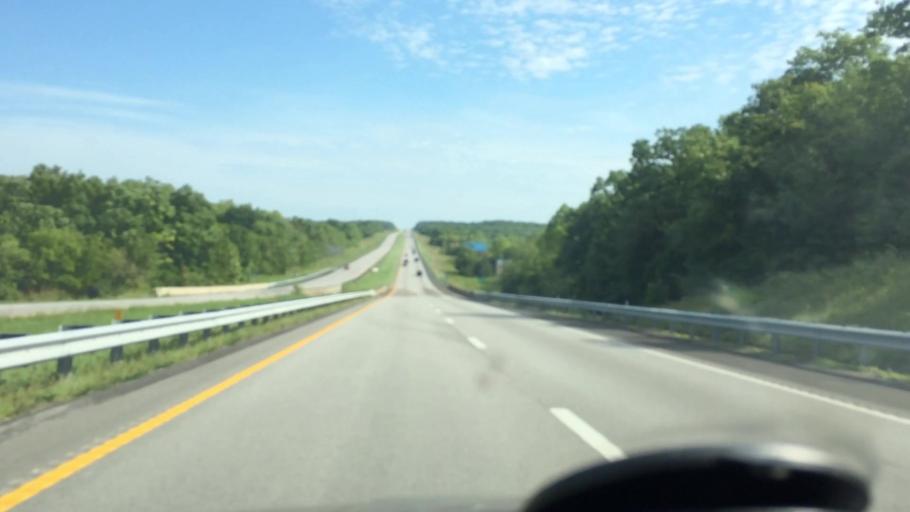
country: US
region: Missouri
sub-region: Webster County
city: Marshfield
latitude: 37.4340
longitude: -92.8771
